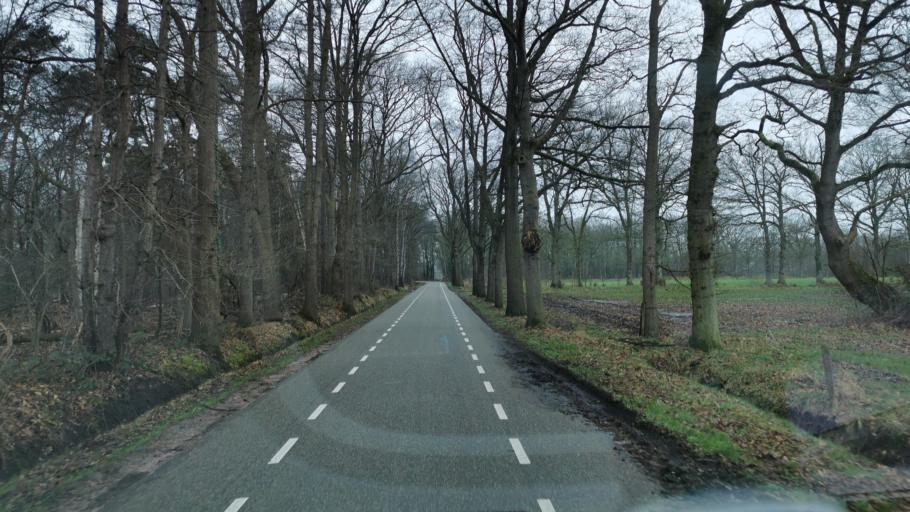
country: NL
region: Overijssel
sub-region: Gemeente Borne
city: Borne
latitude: 52.3278
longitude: 6.7939
